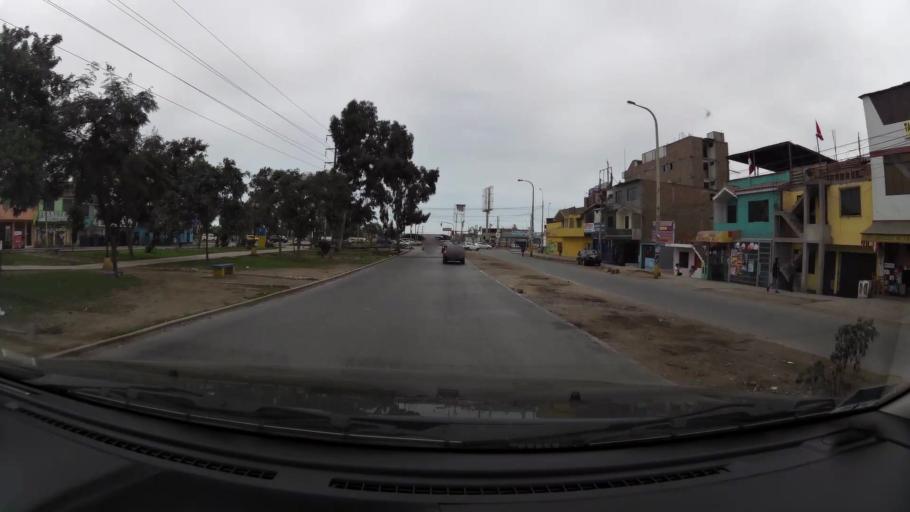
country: PE
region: Lima
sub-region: Lima
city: Surco
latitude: -12.1975
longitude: -76.9568
